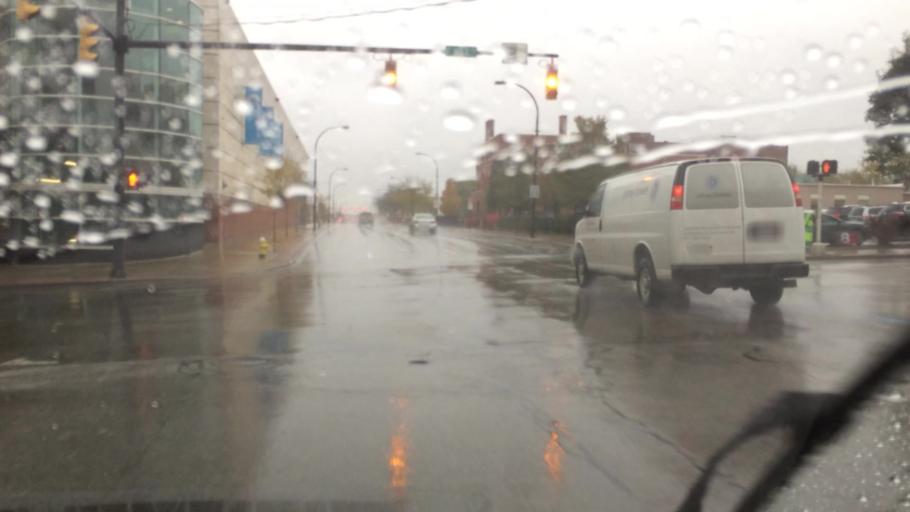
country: US
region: Ohio
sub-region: Summit County
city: Akron
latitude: 41.0818
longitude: -81.5156
